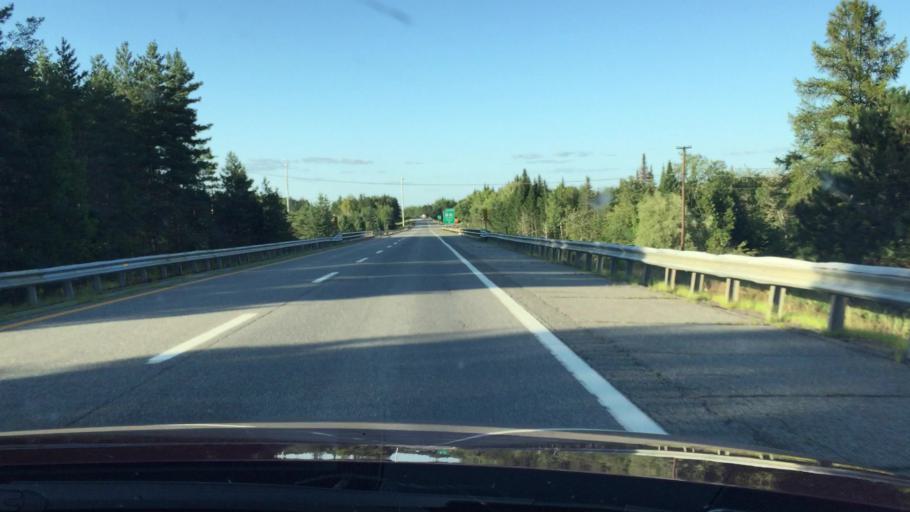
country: US
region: Maine
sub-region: Penobscot County
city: Patten
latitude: 45.8658
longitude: -68.4169
